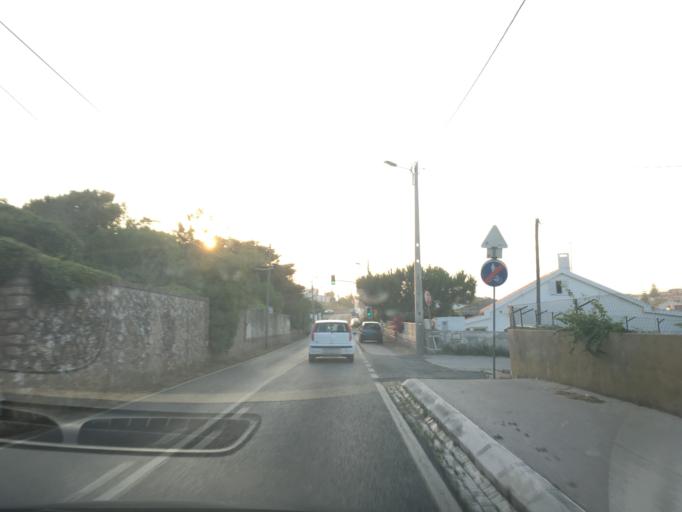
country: PT
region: Lisbon
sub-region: Sintra
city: Colares
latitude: 38.8358
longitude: -9.4576
